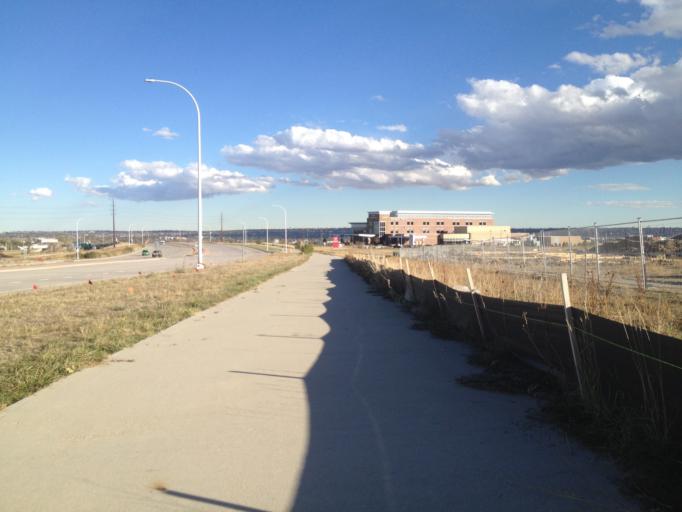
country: US
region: Colorado
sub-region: Broomfield County
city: Broomfield
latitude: 39.9123
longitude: -105.0948
